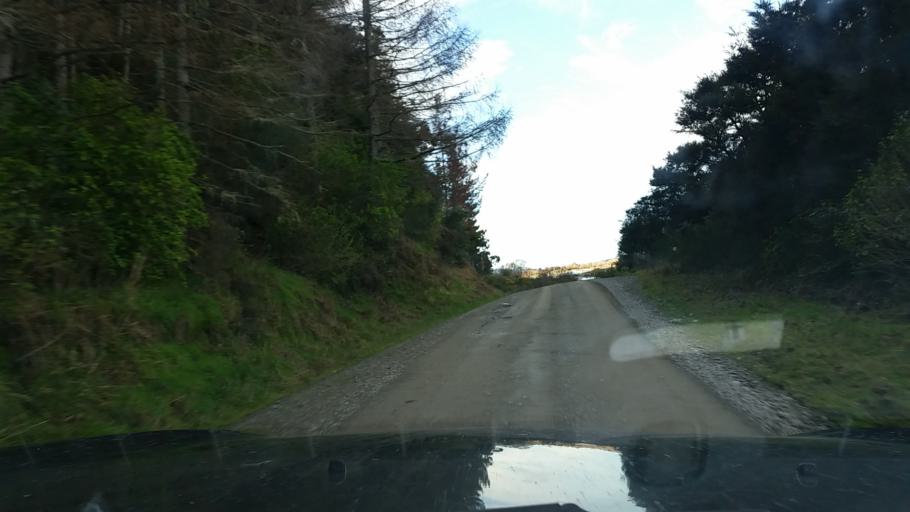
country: NZ
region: Nelson
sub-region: Nelson City
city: Nelson
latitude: -41.5759
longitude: 173.4396
